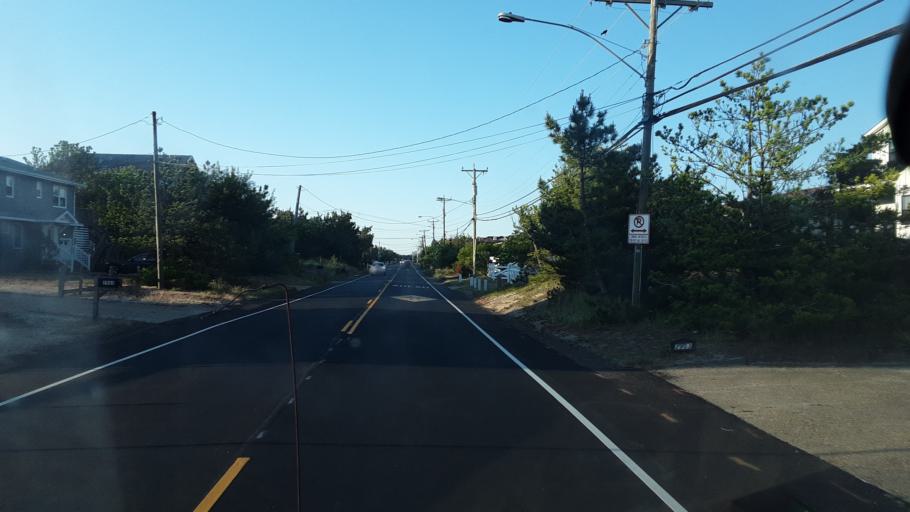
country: US
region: Virginia
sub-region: City of Virginia Beach
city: Virginia Beach
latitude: 36.7265
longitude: -75.9378
